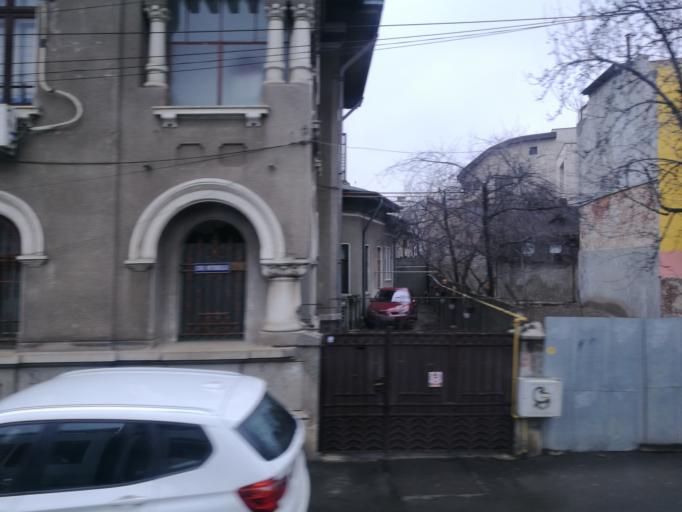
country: RO
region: Bucuresti
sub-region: Municipiul Bucuresti
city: Bucharest
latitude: 44.4501
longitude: 26.1178
